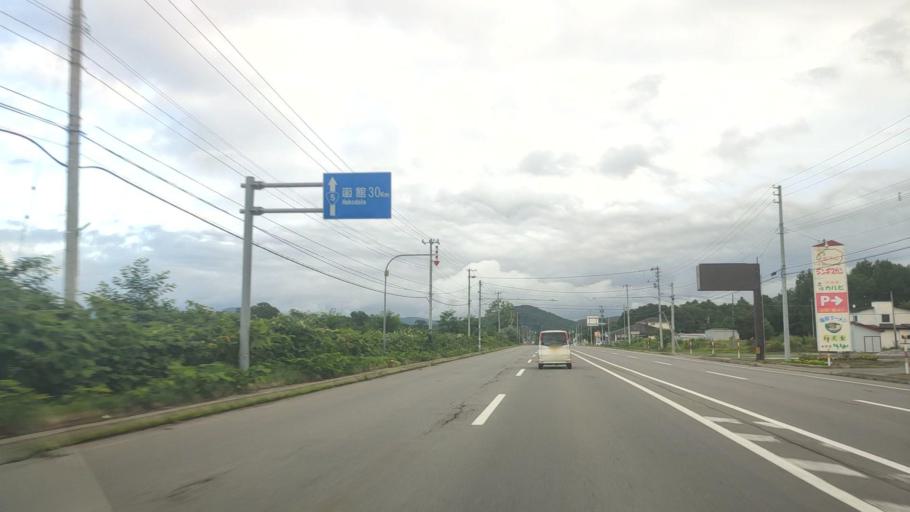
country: JP
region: Hokkaido
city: Nanae
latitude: 42.0063
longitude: 140.6322
